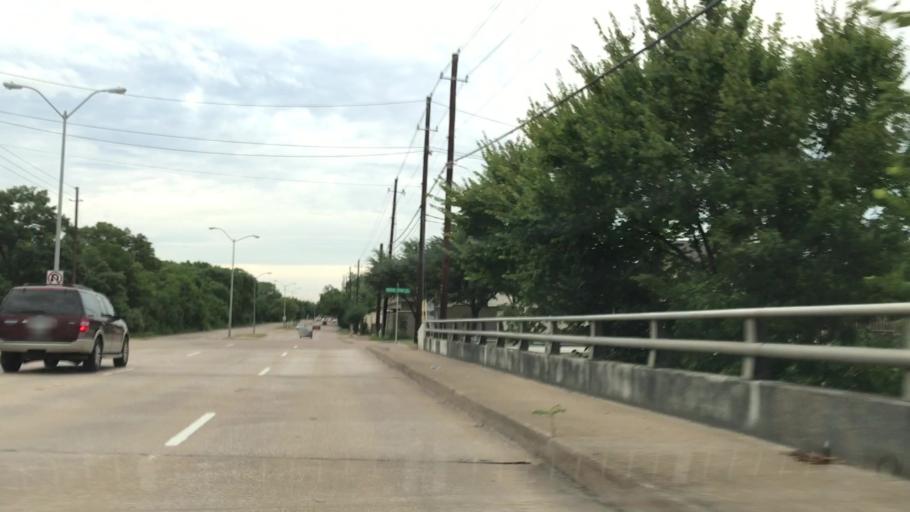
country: US
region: Texas
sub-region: Dallas County
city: Addison
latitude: 32.9274
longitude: -96.7862
